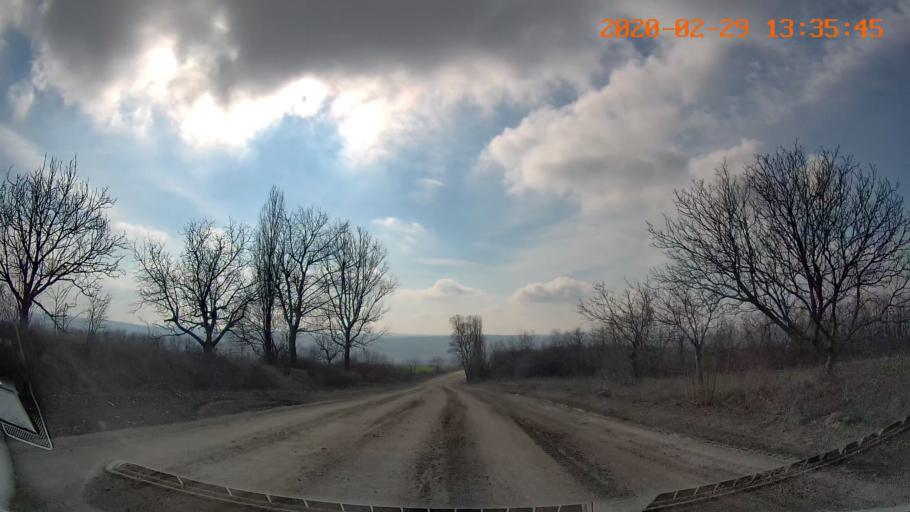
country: MD
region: Telenesti
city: Camenca
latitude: 47.8645
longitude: 28.6109
